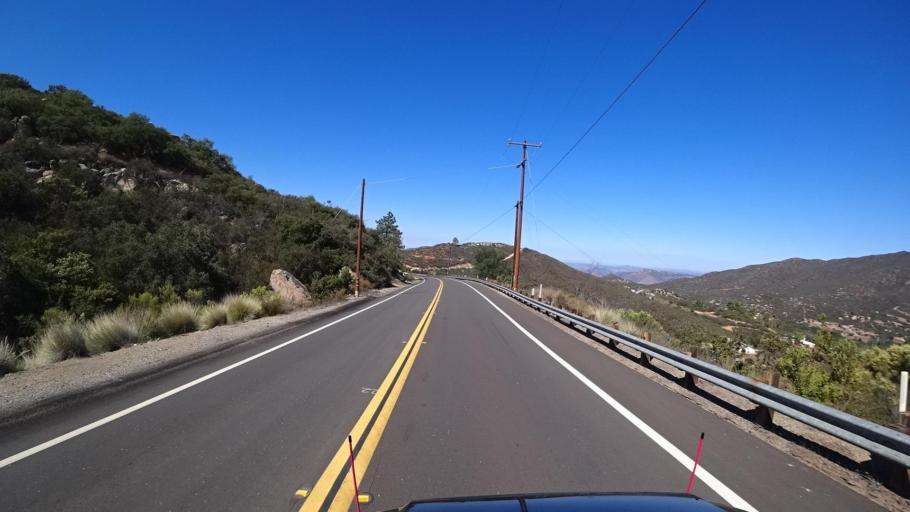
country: US
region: California
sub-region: San Diego County
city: Jamul
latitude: 32.7341
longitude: -116.8002
